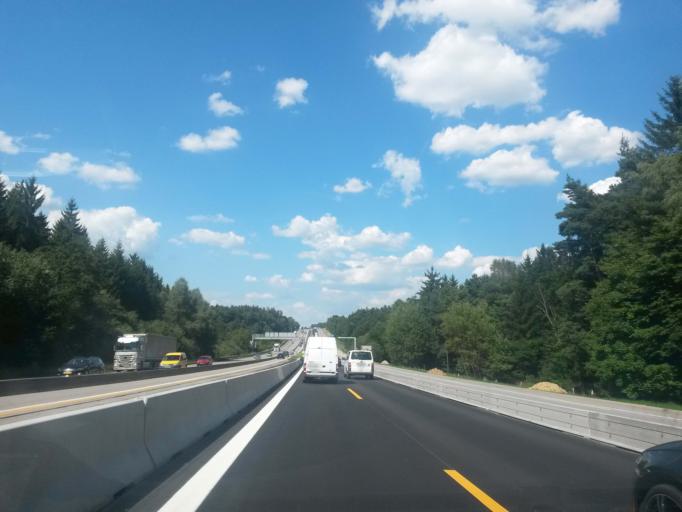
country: DE
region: Bavaria
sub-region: Upper Bavaria
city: Paunzhausen
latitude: 48.4814
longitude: 11.5877
